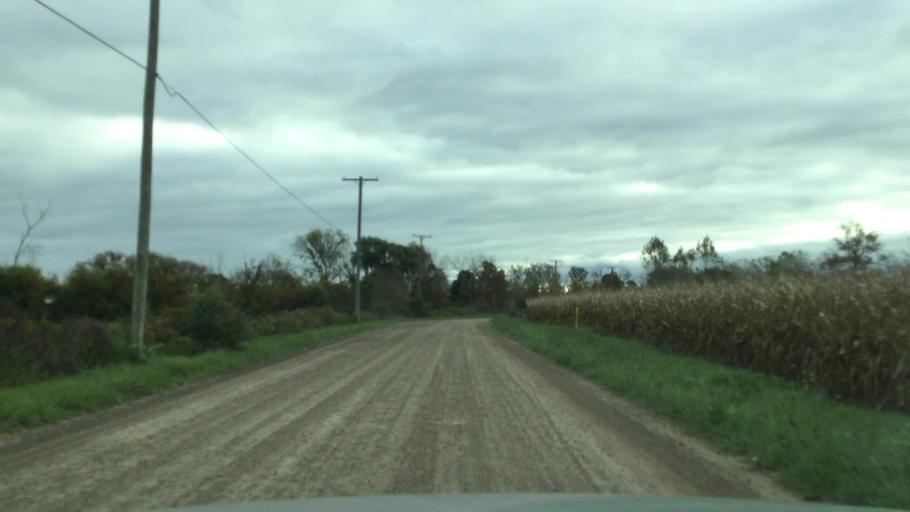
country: US
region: Michigan
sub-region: Macomb County
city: Richmond
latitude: 42.8227
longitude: -82.7434
